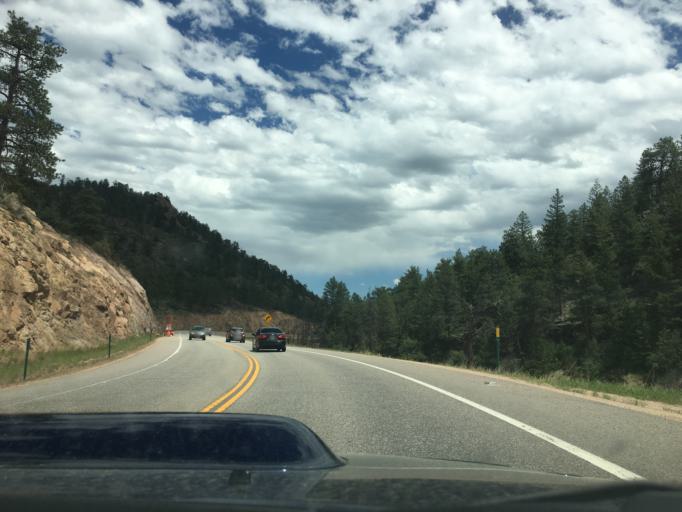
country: US
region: Colorado
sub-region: Boulder County
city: Lyons
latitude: 40.2840
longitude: -105.3681
